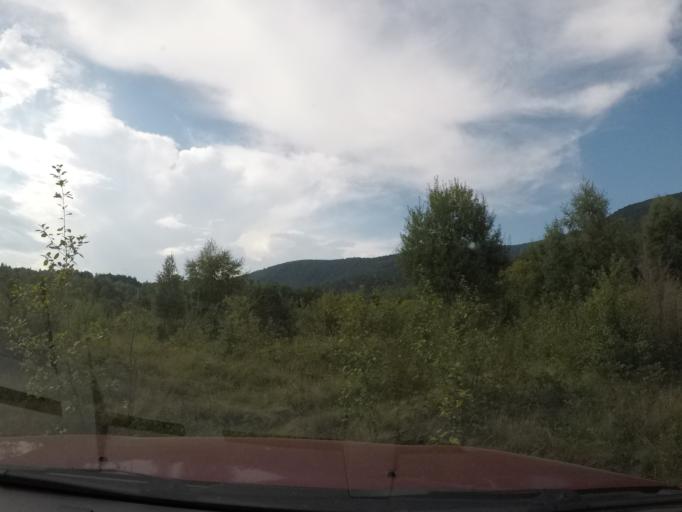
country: PL
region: Subcarpathian Voivodeship
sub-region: Powiat bieszczadzki
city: Lutowiska
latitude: 49.0371
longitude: 22.6375
